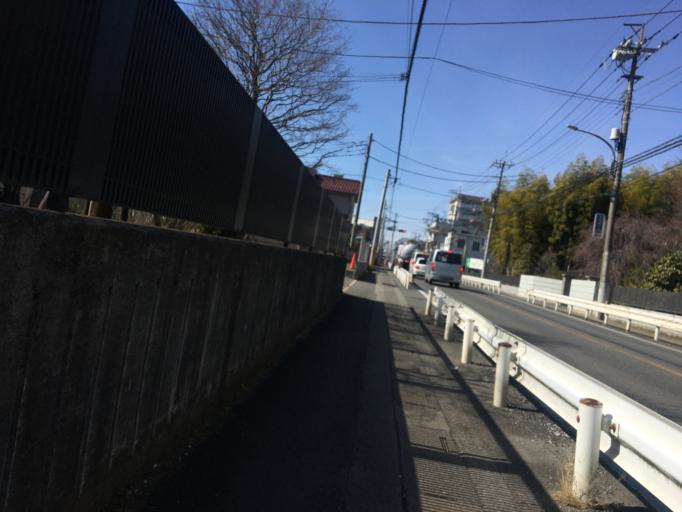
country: JP
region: Saitama
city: Shiki
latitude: 35.8024
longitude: 139.5664
